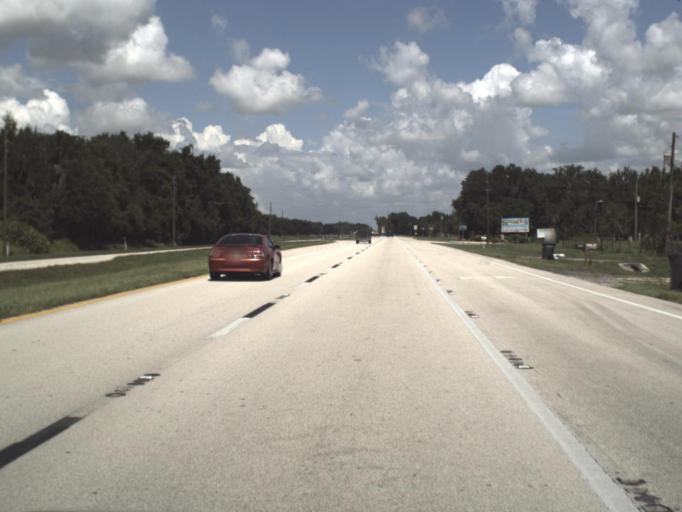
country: US
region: Florida
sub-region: Polk County
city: Fort Meade
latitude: 27.7269
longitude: -81.8013
